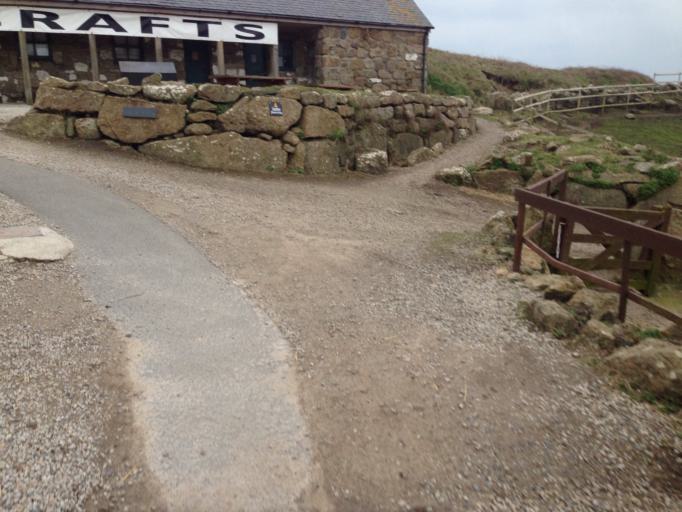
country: GB
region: England
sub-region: Cornwall
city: Sennen
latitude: 50.0627
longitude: -5.7110
